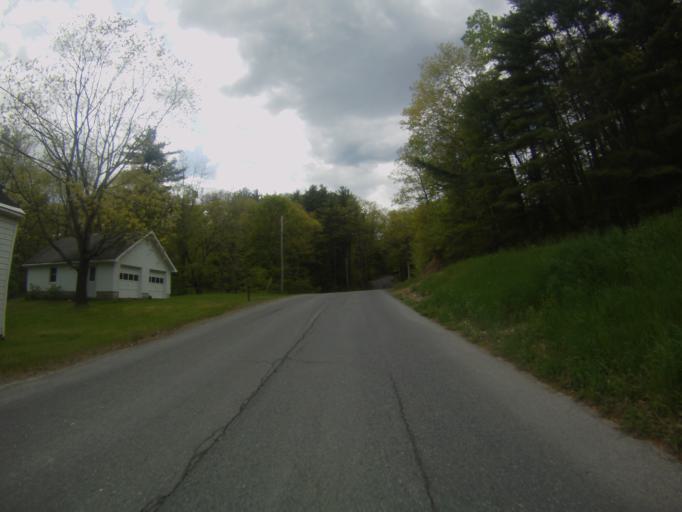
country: US
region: New York
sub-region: Essex County
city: Ticonderoga
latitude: 43.8825
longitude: -73.4691
